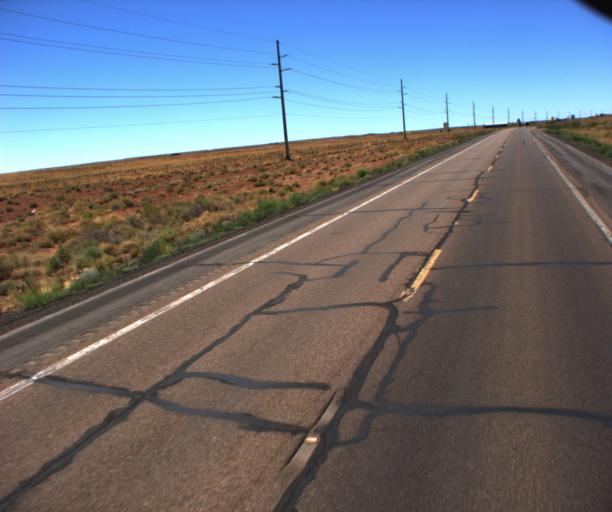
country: US
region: Arizona
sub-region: Navajo County
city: Winslow
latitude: 35.0031
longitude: -110.7047
